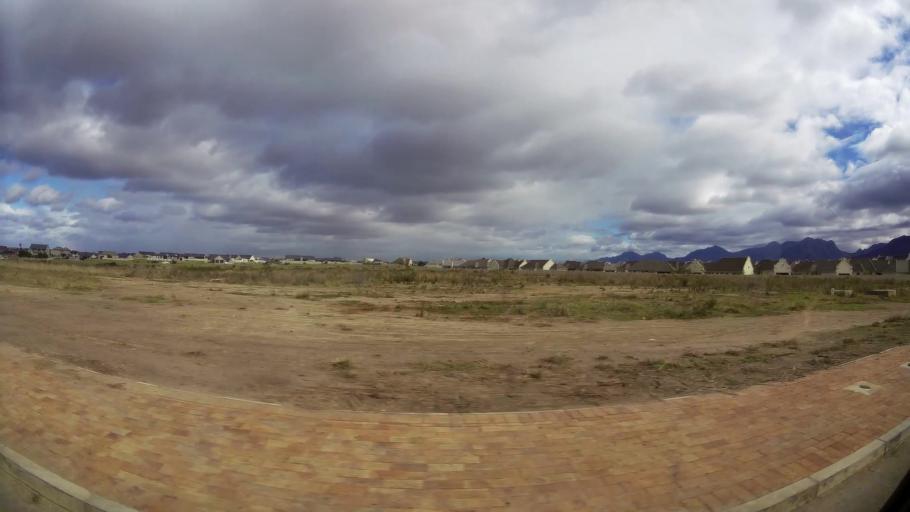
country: ZA
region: Western Cape
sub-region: Eden District Municipality
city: George
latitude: -33.9856
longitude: 22.4985
